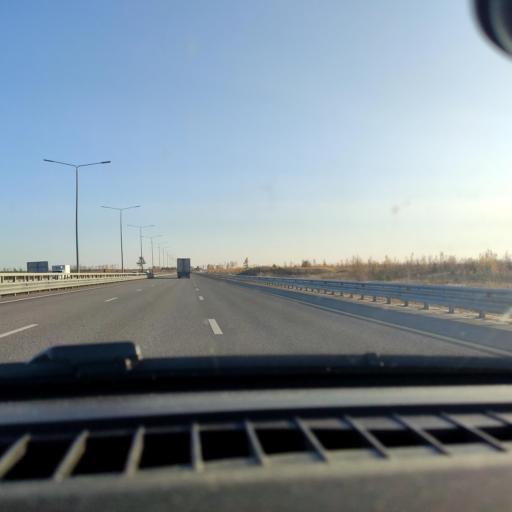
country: RU
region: Voronezj
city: Somovo
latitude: 51.7732
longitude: 39.3014
